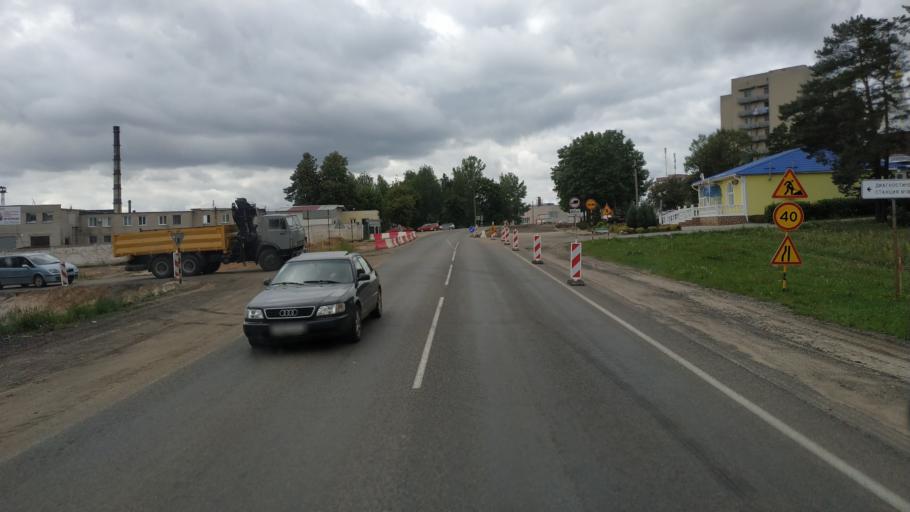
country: BY
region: Mogilev
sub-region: Mahilyowski Rayon
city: Veyno
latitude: 53.8793
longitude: 30.4114
